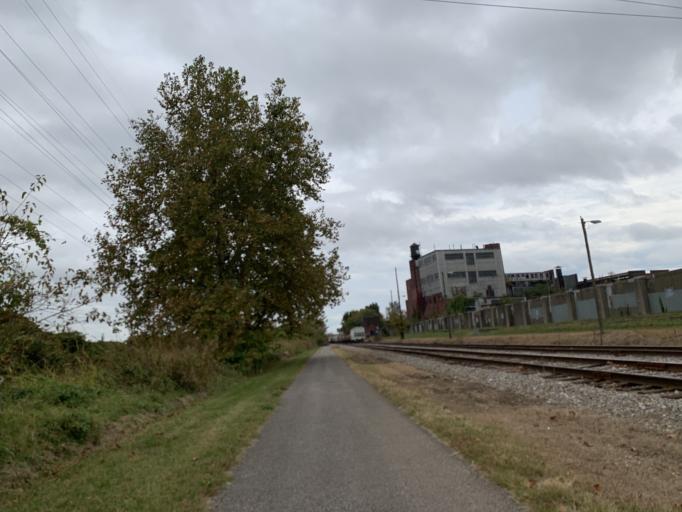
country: US
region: Kentucky
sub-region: Jefferson County
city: Louisville
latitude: 38.2704
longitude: -85.7797
